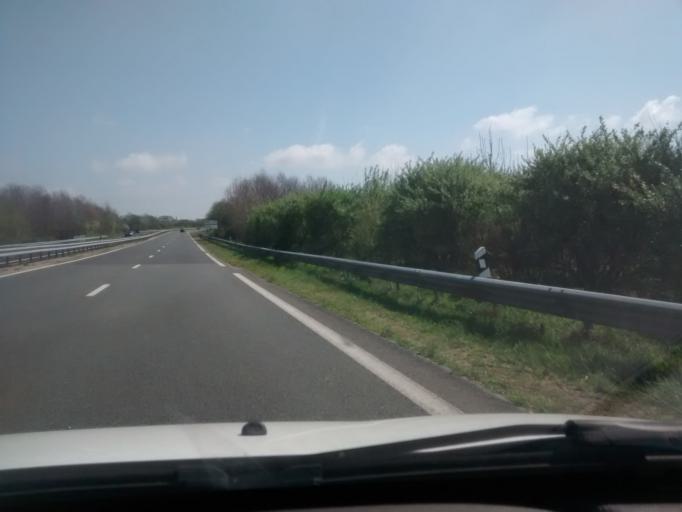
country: FR
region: Brittany
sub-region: Departement des Cotes-d'Armor
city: Cavan
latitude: 48.6837
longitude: -3.3609
